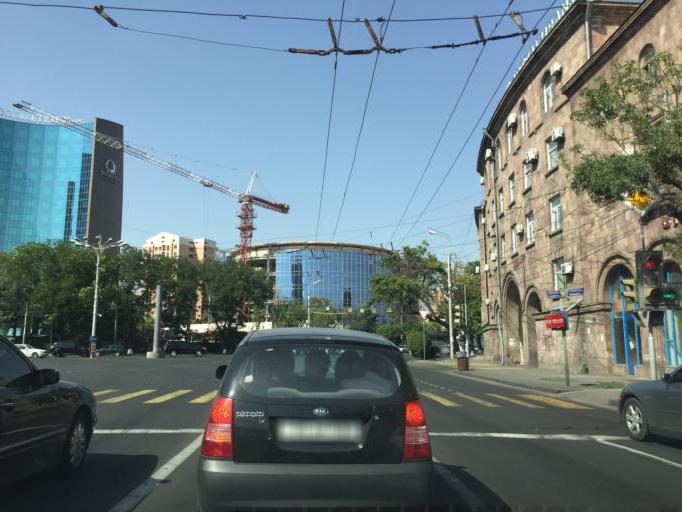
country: AM
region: Yerevan
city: Yerevan
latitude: 40.1705
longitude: 44.5083
